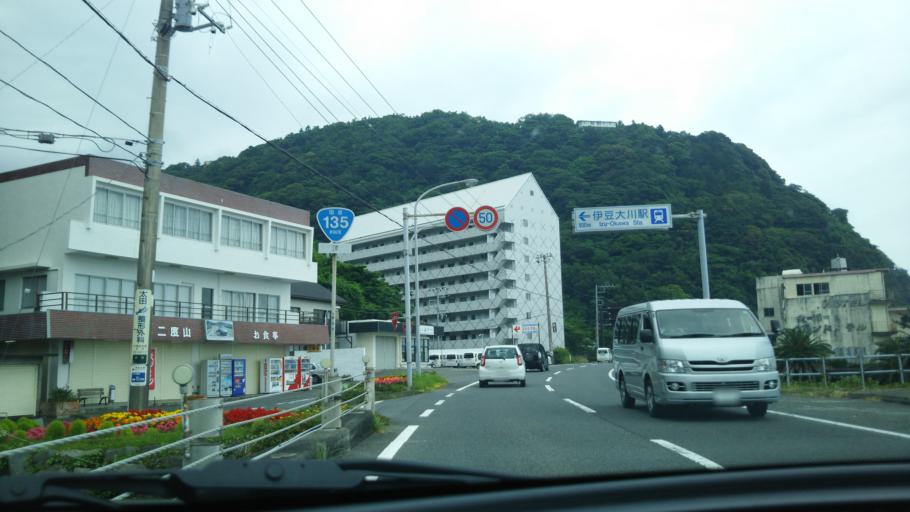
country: JP
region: Shizuoka
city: Ito
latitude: 34.8417
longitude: 139.0765
